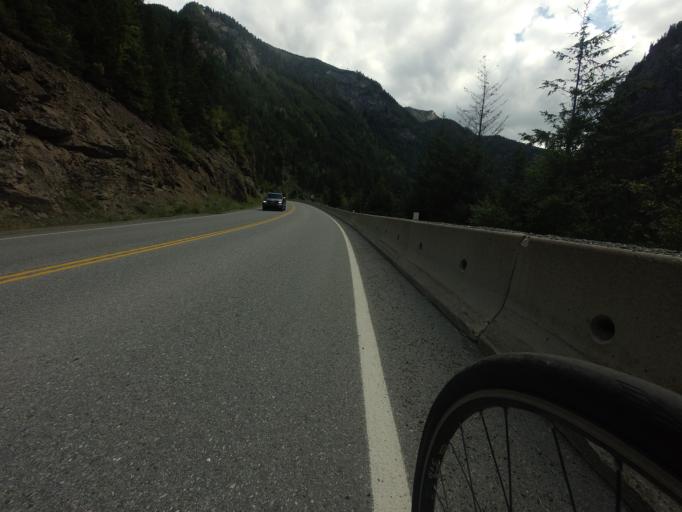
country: CA
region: British Columbia
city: Lillooet
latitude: 50.6456
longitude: -122.0700
